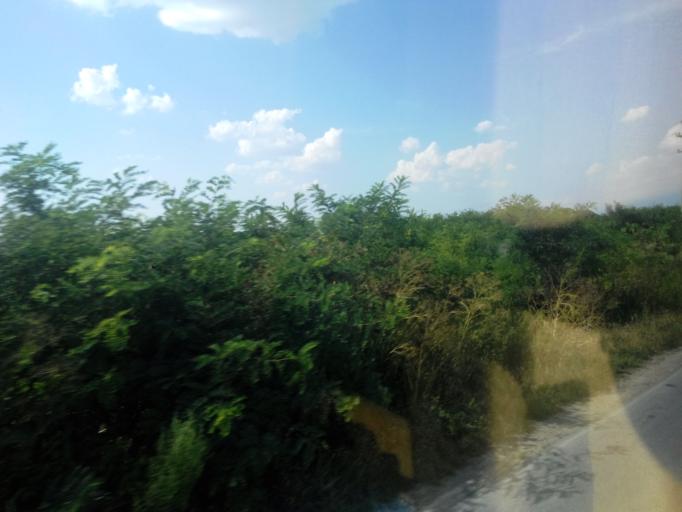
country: RO
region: Timis
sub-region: Comuna Ghiroda
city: Giarmata-Vii
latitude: 45.8247
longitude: 21.2765
